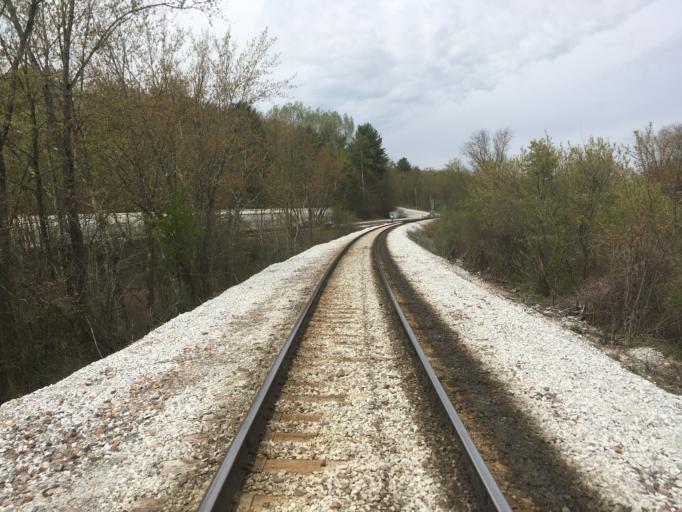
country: US
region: Vermont
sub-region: Rutland County
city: Brandon
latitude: 43.7184
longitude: -73.0531
